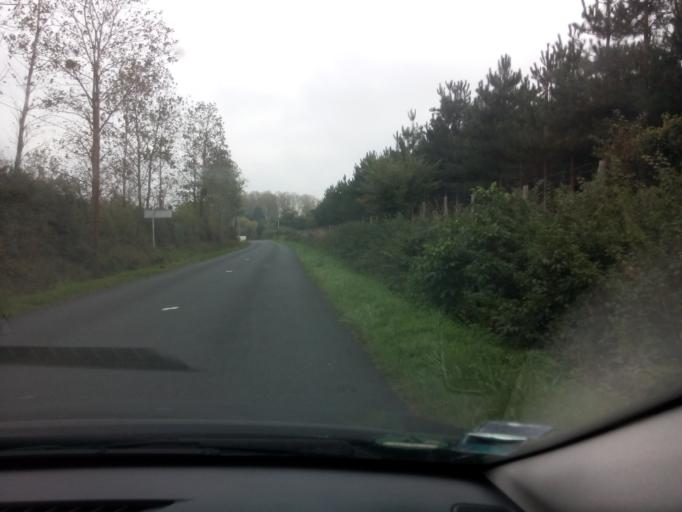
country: FR
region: Pays de la Loire
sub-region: Departement de Maine-et-Loire
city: Soulaire-et-Bourg
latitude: 47.6175
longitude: -0.5245
